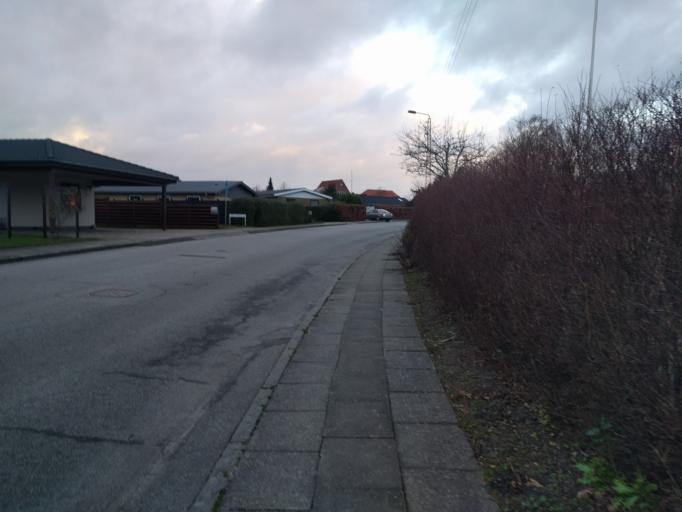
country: DK
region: Central Jutland
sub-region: Viborg Kommune
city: Viborg
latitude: 56.4550
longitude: 9.3808
